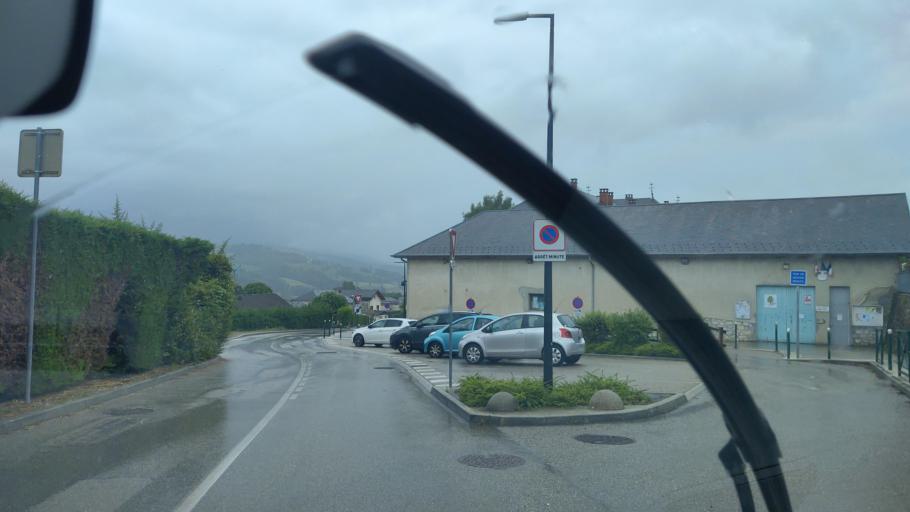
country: FR
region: Rhone-Alpes
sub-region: Departement de la Savoie
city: La Biolle
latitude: 45.7589
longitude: 5.9286
